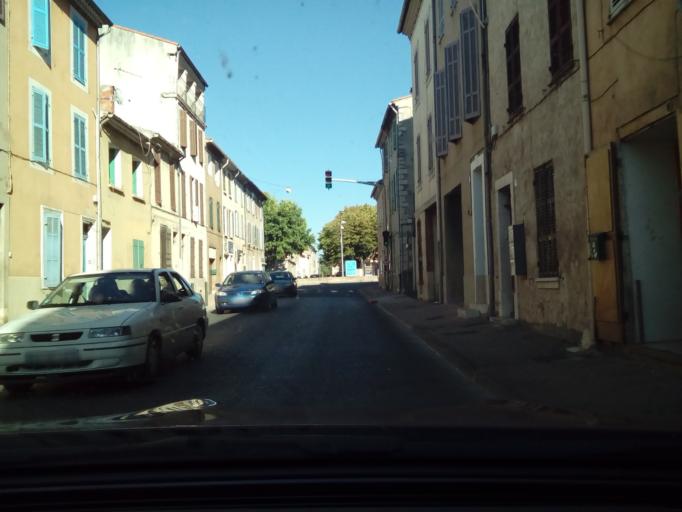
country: FR
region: Provence-Alpes-Cote d'Azur
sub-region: Departement du Var
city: Saint-Maximin-la-Sainte-Baume
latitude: 43.4516
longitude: 5.8613
